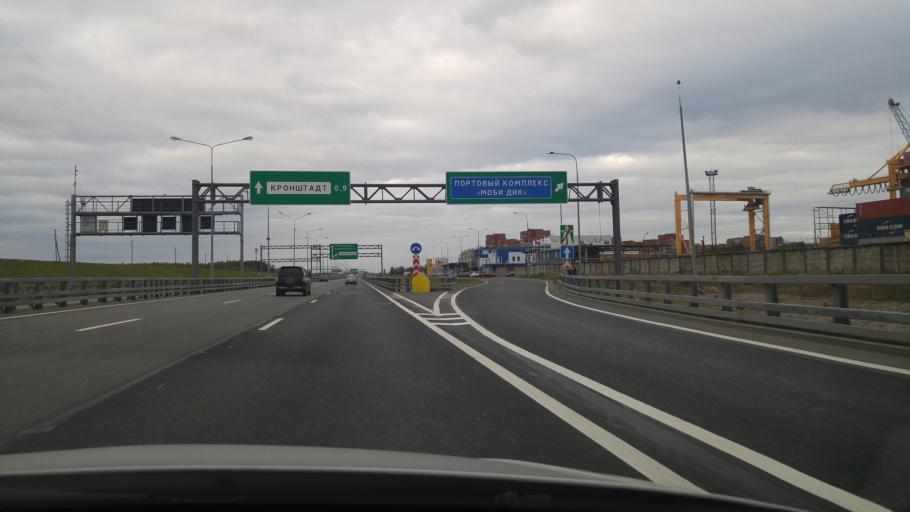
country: RU
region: St.-Petersburg
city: Kronshtadt
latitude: 60.0046
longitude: 29.7075
